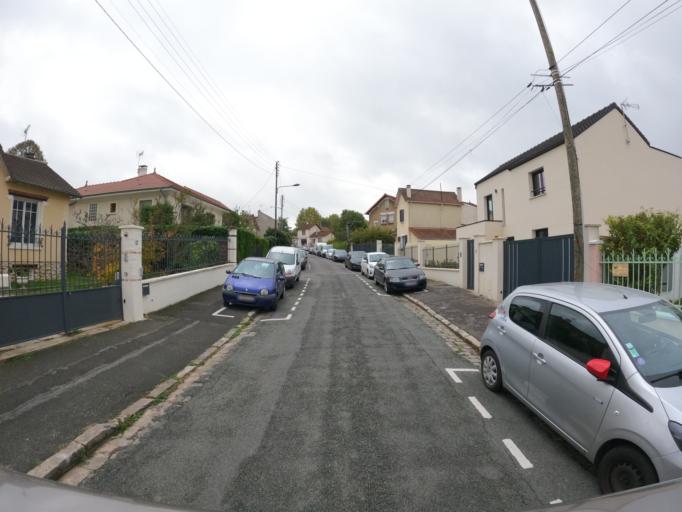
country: FR
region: Ile-de-France
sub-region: Departement du Val-de-Marne
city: Sucy-en-Brie
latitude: 48.7764
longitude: 2.5151
